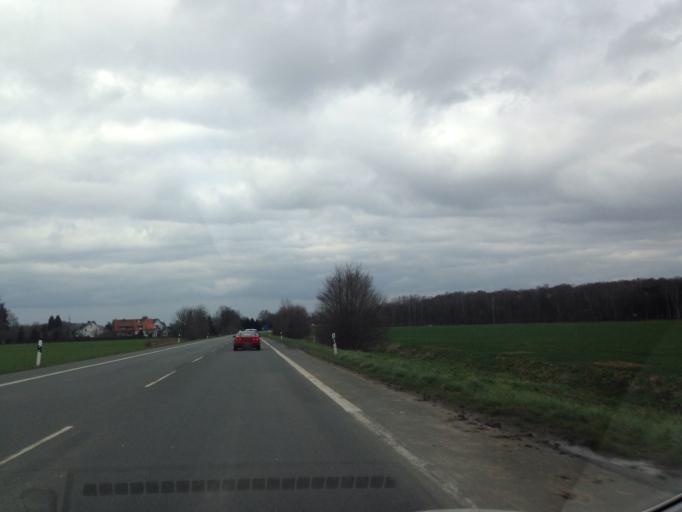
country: DE
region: North Rhine-Westphalia
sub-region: Regierungsbezirk Munster
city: Senden
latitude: 51.8806
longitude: 7.5683
